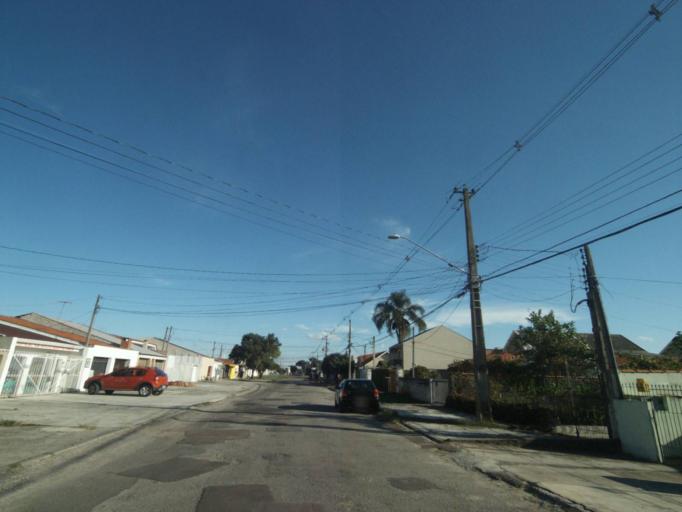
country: BR
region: Parana
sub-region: Pinhais
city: Pinhais
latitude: -25.4585
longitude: -49.2038
